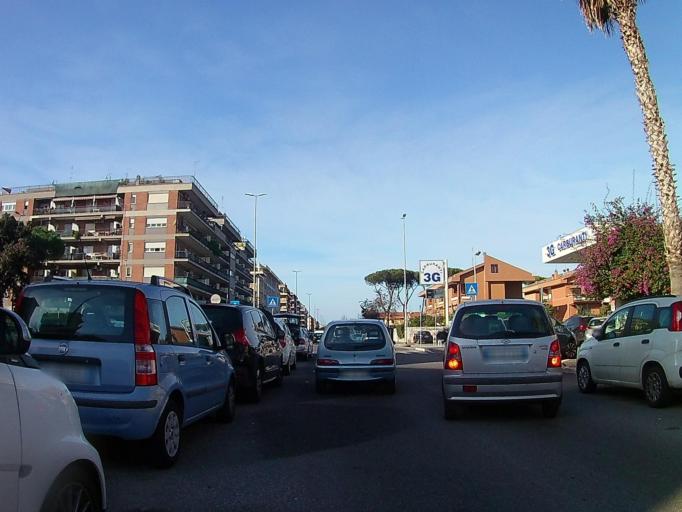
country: IT
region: Latium
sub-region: Citta metropolitana di Roma Capitale
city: Lido di Ostia
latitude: 41.7372
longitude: 12.2929
